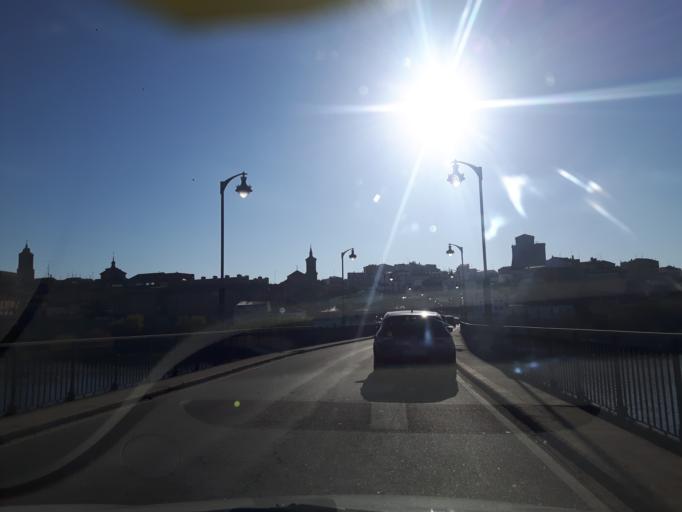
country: ES
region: Castille and Leon
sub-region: Provincia de Salamanca
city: Alba de Tormes
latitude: 40.8258
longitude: -5.5186
